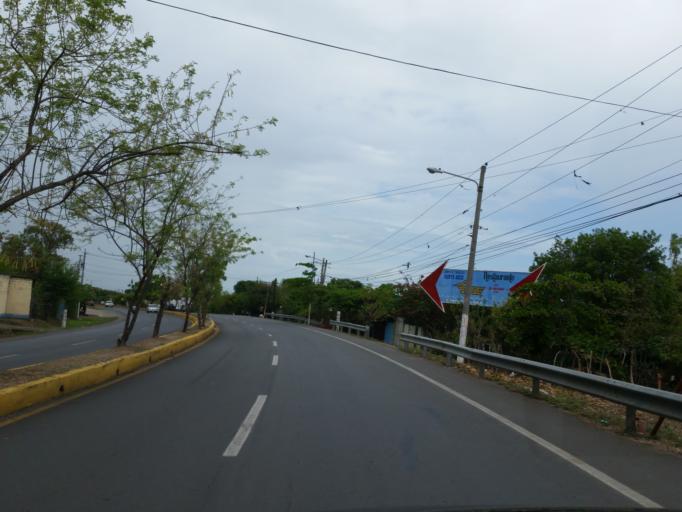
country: NI
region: Granada
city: Granada
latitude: 11.9360
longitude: -85.9726
